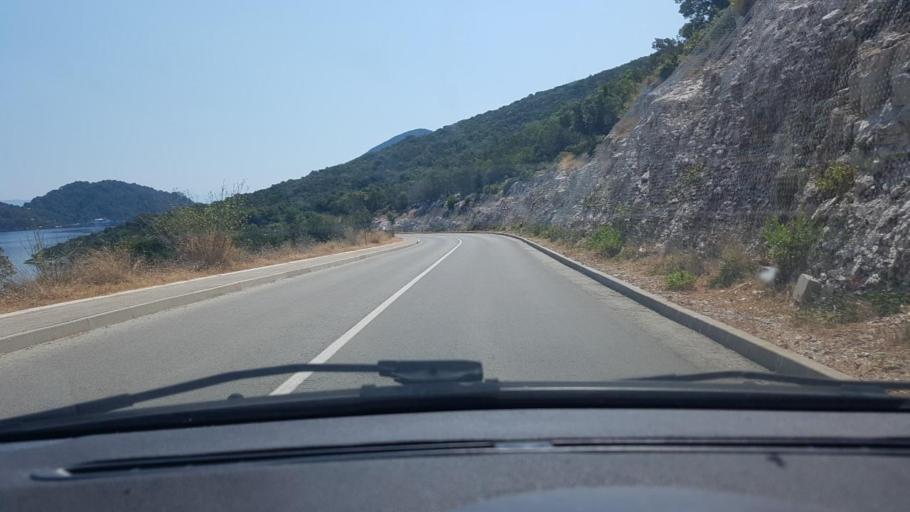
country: HR
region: Dubrovacko-Neretvanska
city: Blato
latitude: 42.7868
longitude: 17.3869
